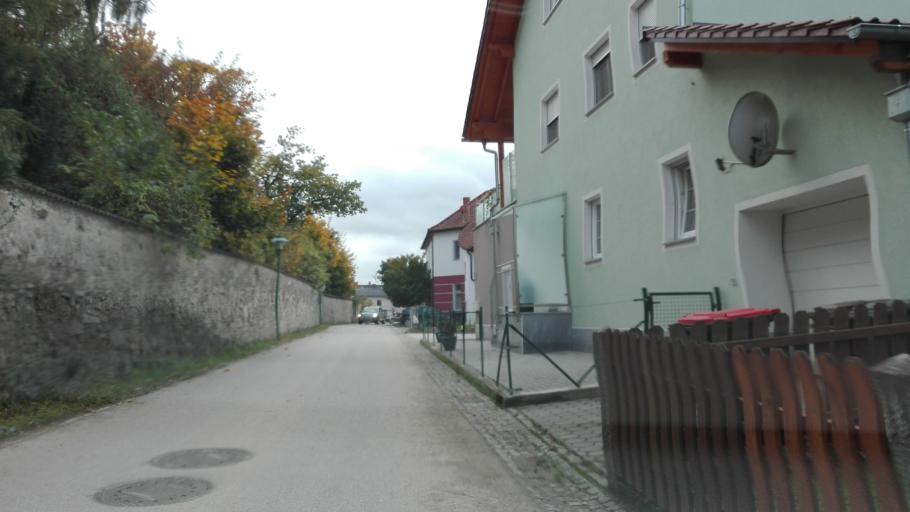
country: AT
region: Upper Austria
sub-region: Politischer Bezirk Urfahr-Umgebung
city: Feldkirchen an der Donau
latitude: 48.3391
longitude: 14.0004
